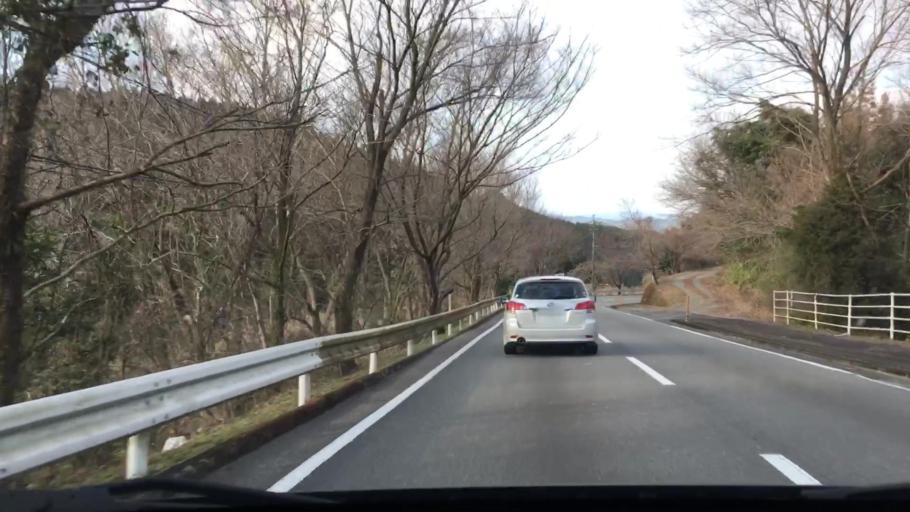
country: JP
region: Miyazaki
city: Miyazaki-shi
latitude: 31.8033
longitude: 131.3015
